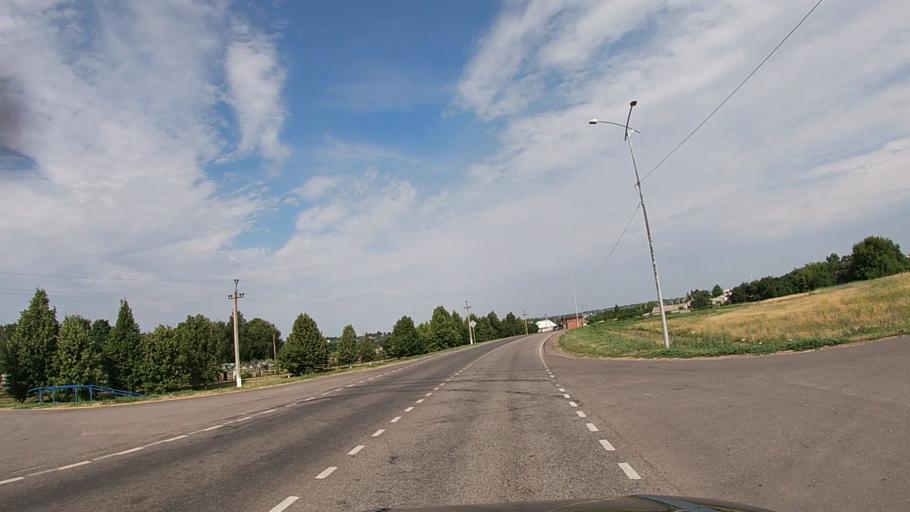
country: RU
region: Belgorod
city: Krasnaya Yaruga
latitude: 50.7986
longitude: 35.6799
